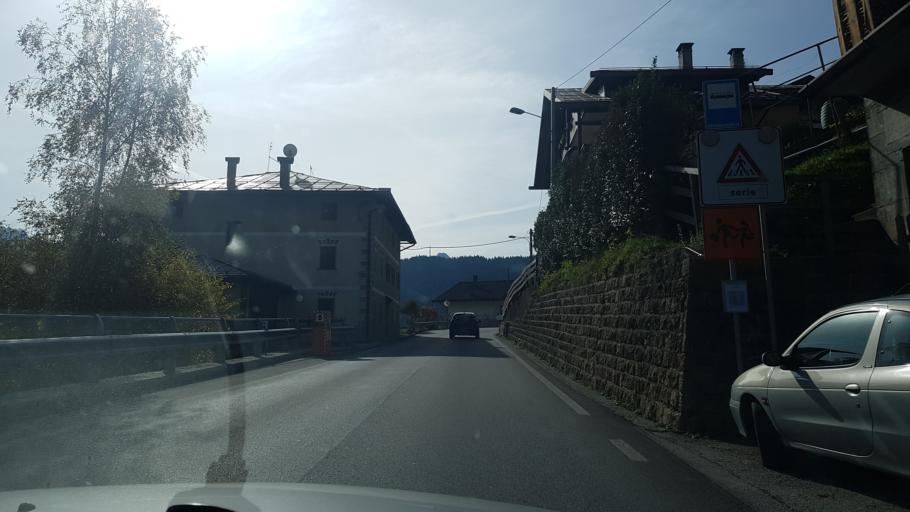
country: IT
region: Veneto
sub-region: Provincia di Belluno
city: Candide
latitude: 46.5913
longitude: 12.5190
